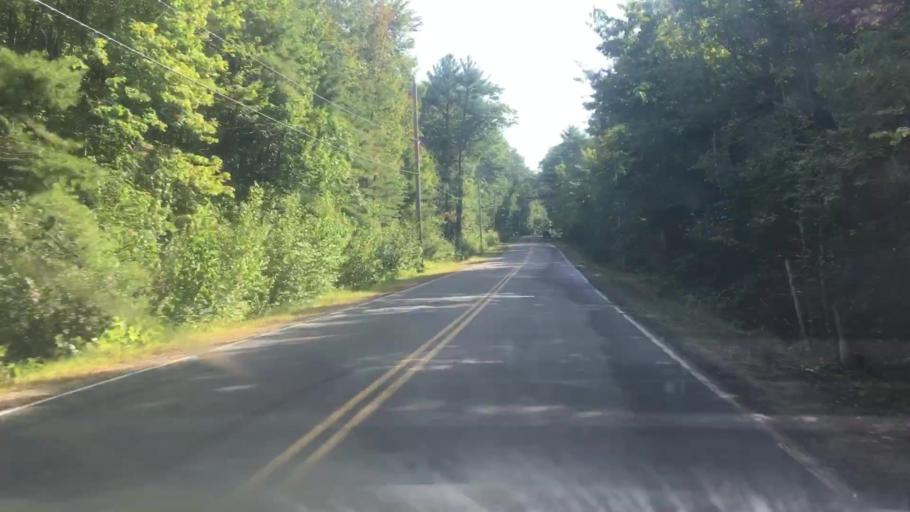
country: US
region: Maine
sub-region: Kennebec County
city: Pittston
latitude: 44.1671
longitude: -69.7868
